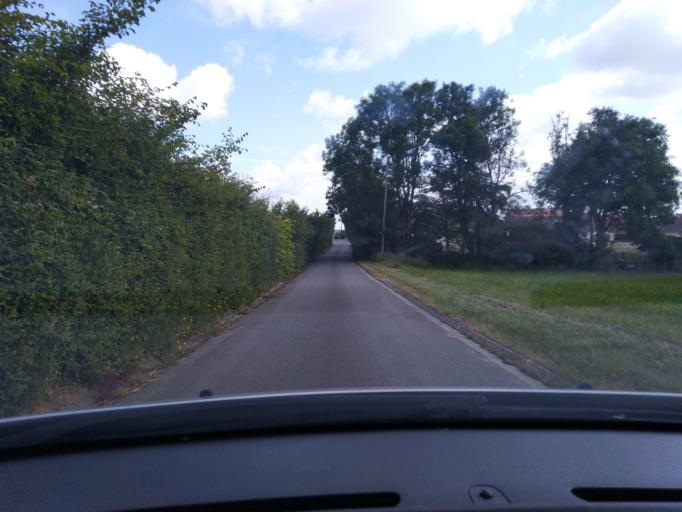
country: FR
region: Nord-Pas-de-Calais
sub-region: Departement du Pas-de-Calais
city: Ferques
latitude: 50.8395
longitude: 1.7557
